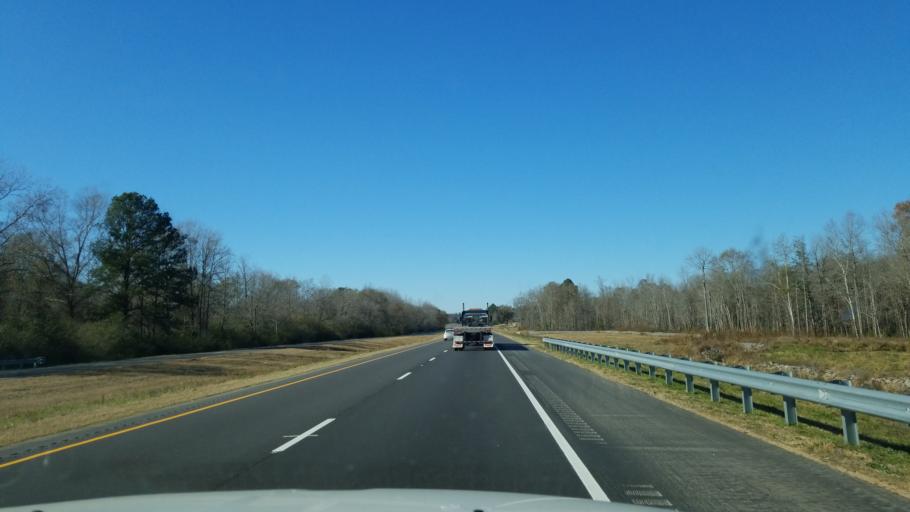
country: US
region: Alabama
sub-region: Pickens County
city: Gordo
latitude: 33.3457
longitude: -87.9483
